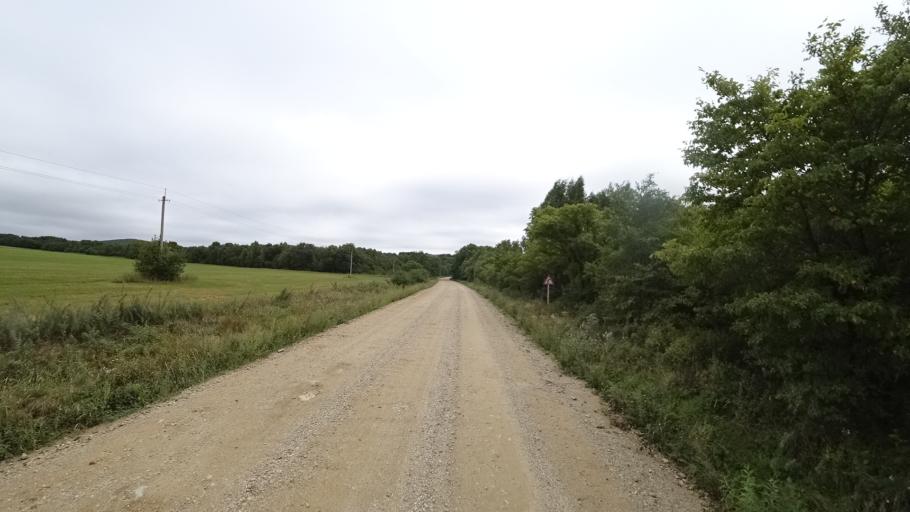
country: RU
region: Primorskiy
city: Lyalichi
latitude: 44.0682
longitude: 132.4774
